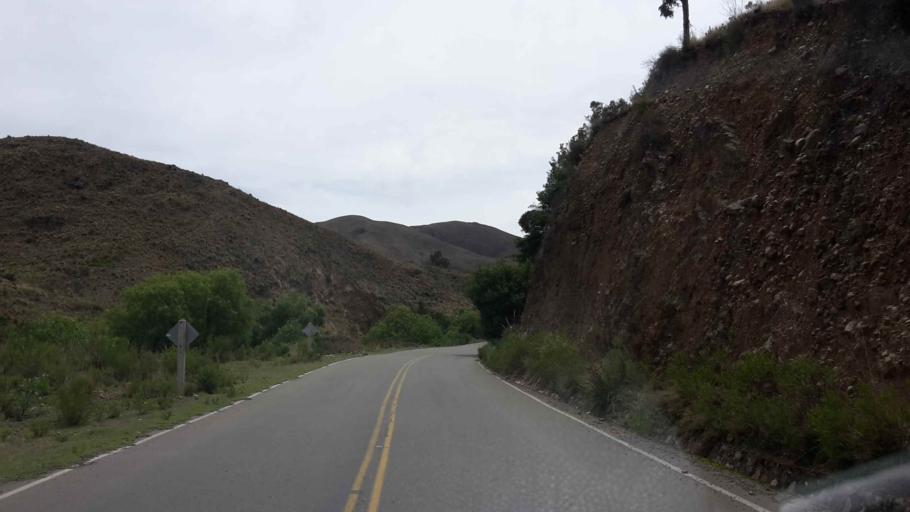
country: BO
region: Cochabamba
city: Colomi
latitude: -17.4010
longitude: -65.8067
